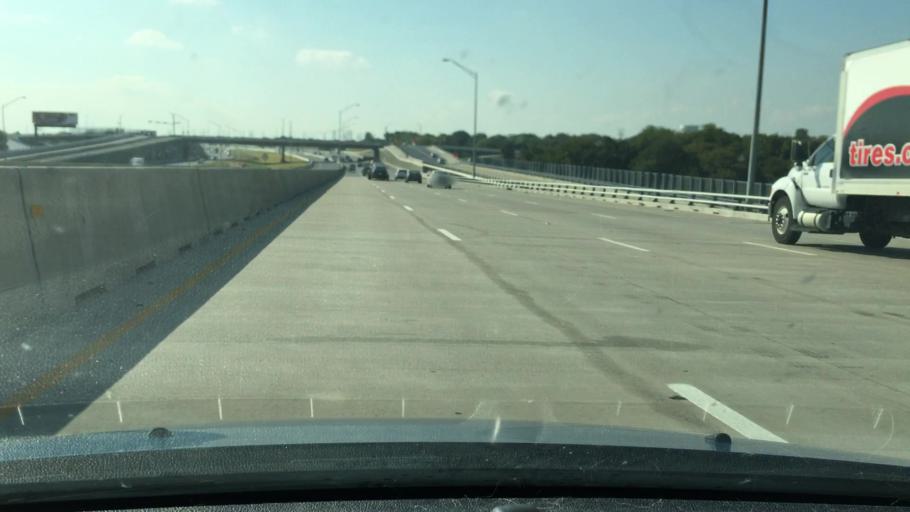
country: US
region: Texas
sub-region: Denton County
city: Highland Village
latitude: 33.0882
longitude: -97.0281
